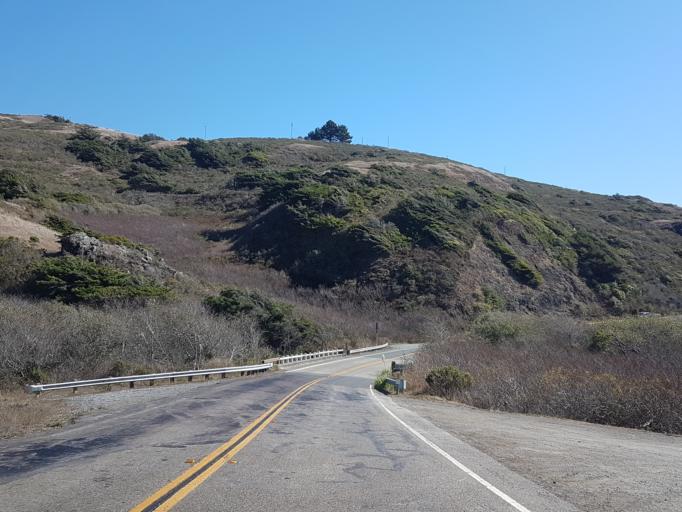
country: US
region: California
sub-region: Sonoma County
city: Monte Rio
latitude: 38.4712
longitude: -123.1543
